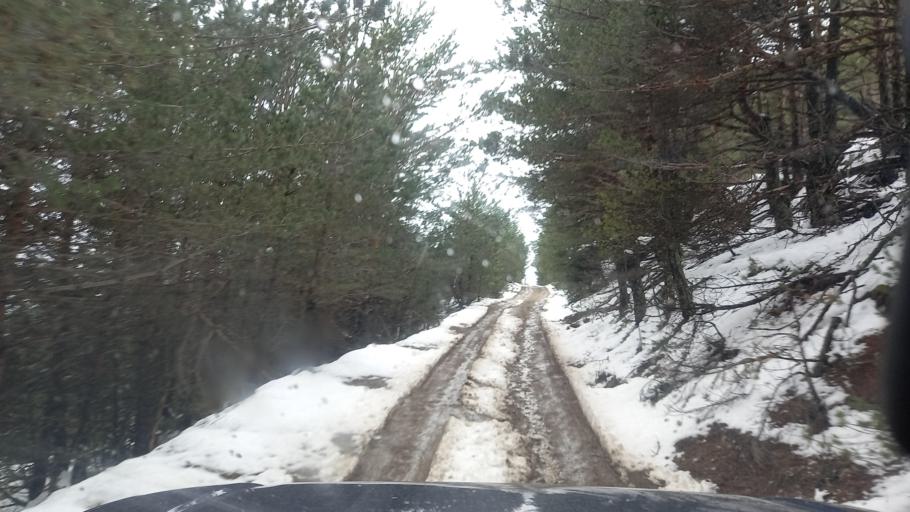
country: RU
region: North Ossetia
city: Mizur
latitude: 42.8096
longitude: 43.9586
